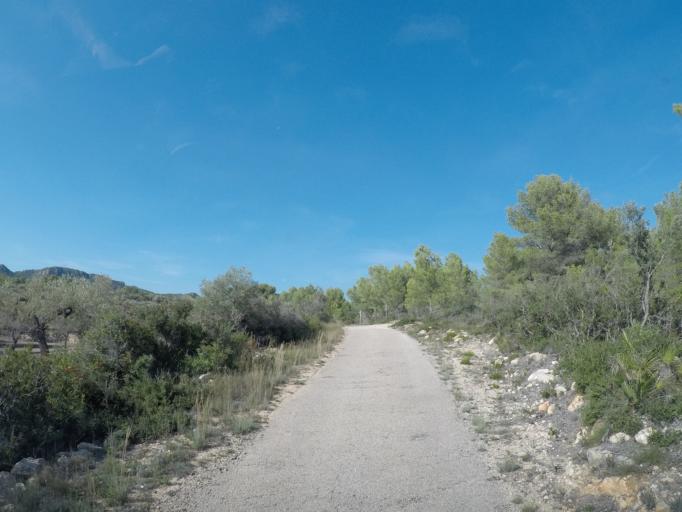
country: ES
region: Catalonia
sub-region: Provincia de Tarragona
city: El Perello
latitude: 40.9112
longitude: 0.7237
